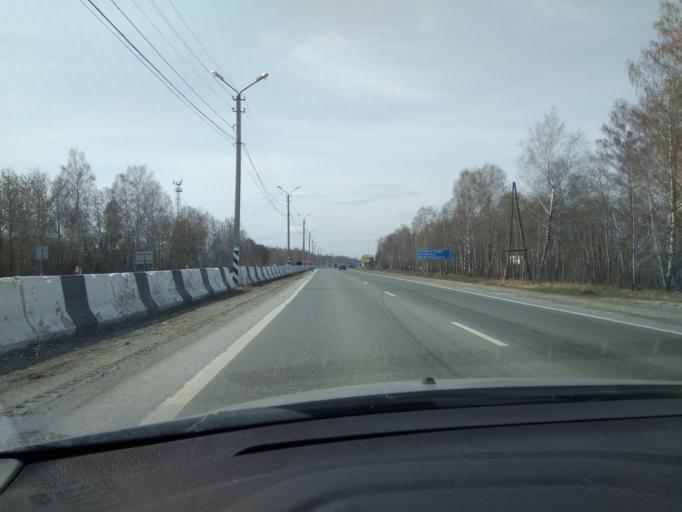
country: RU
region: Tjumen
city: Moskovskiy
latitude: 57.1146
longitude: 65.4162
